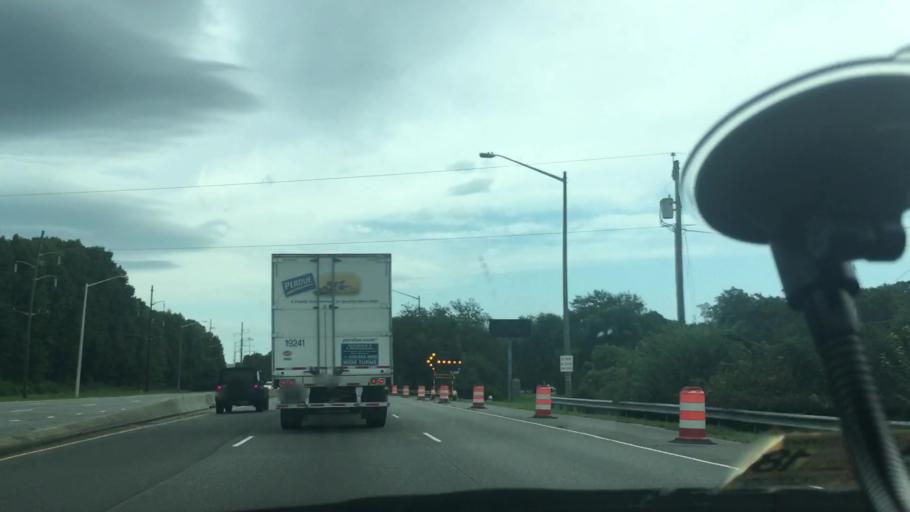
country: US
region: Virginia
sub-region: City of Norfolk
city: Norfolk
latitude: 36.8918
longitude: -76.1692
